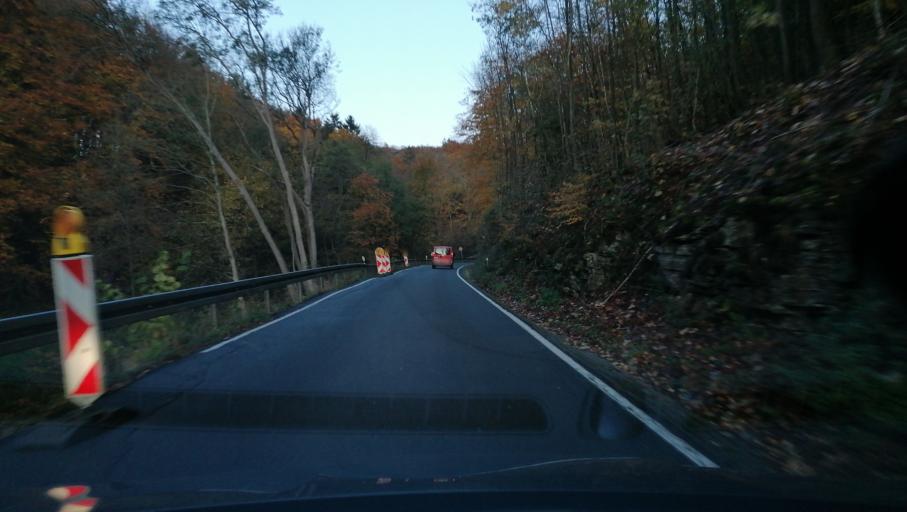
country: DE
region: North Rhine-Westphalia
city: Wetter (Ruhr)
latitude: 51.3973
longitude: 7.3736
